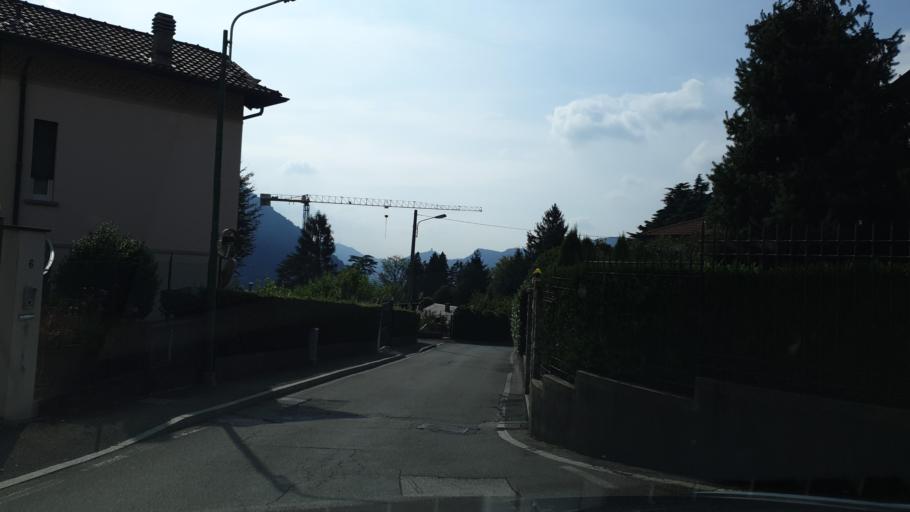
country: IT
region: Lombardy
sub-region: Provincia di Como
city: Cernobbio
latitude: 45.8420
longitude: 9.0692
